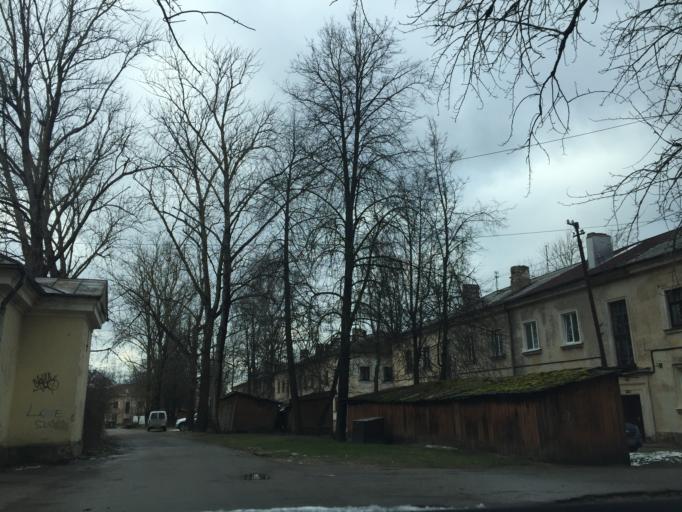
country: LV
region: Riga
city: Jaunciems
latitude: 56.9846
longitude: 24.1986
